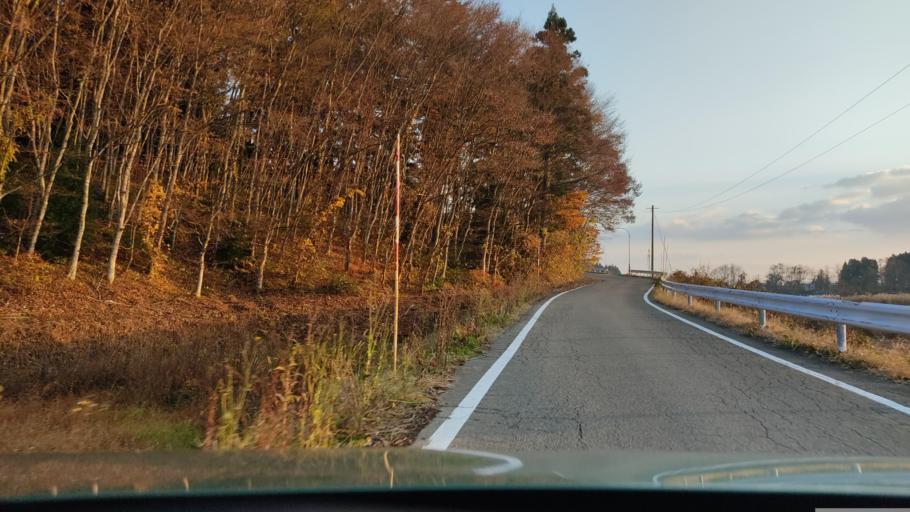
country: JP
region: Akita
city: Omagari
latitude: 39.4213
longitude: 140.5853
